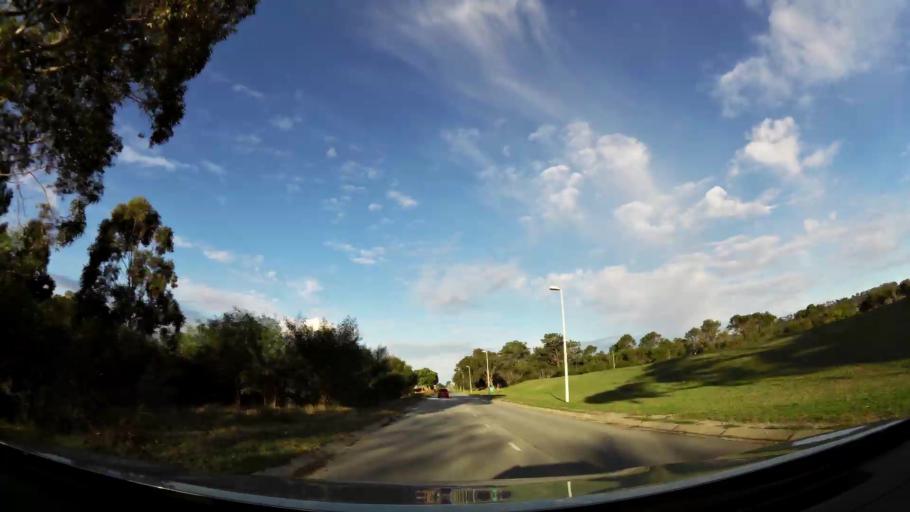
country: ZA
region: Eastern Cape
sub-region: Nelson Mandela Bay Metropolitan Municipality
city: Port Elizabeth
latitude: -33.9760
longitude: 25.5078
